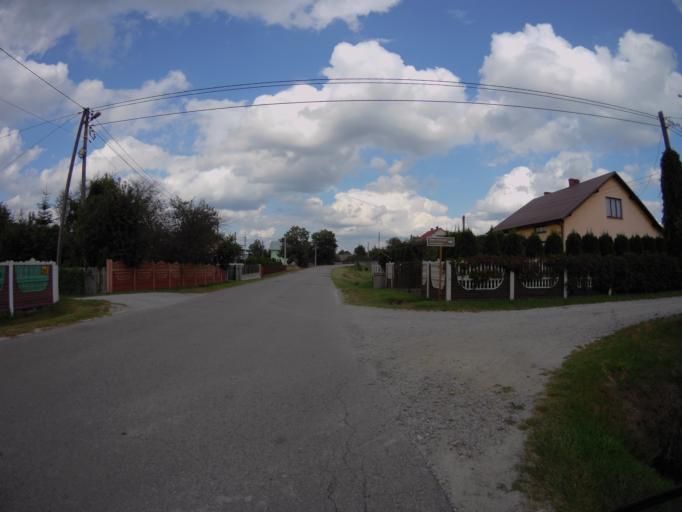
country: PL
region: Subcarpathian Voivodeship
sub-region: Powiat lezajski
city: Brzoza Krolewska
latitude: 50.2399
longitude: 22.3264
